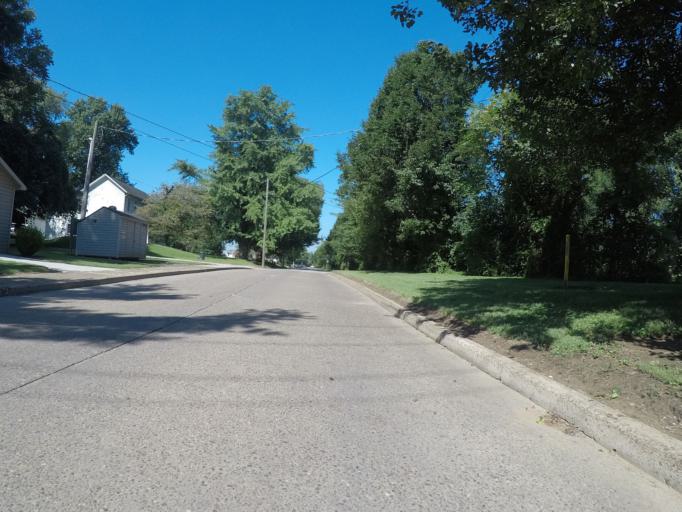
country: US
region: West Virginia
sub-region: Wayne County
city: Ceredo
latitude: 38.3993
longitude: -82.5642
